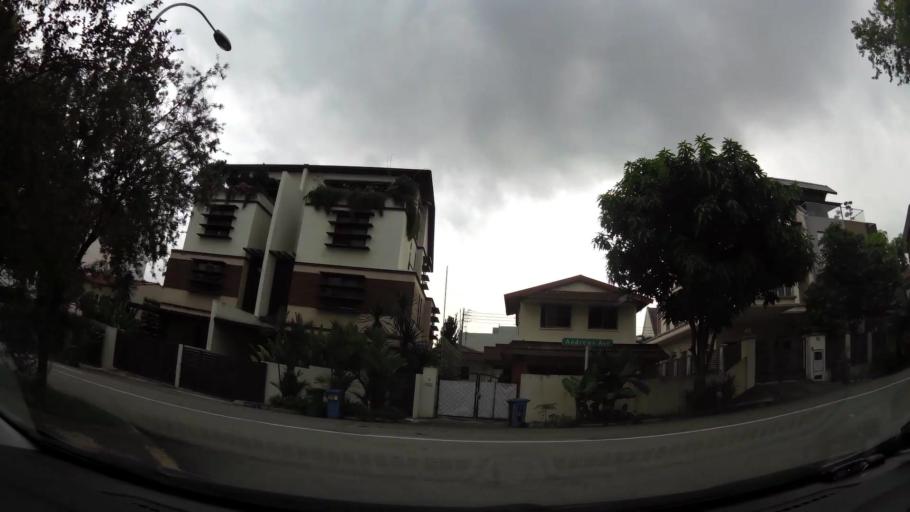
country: MY
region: Johor
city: Kampung Pasir Gudang Baru
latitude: 1.4585
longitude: 103.8374
